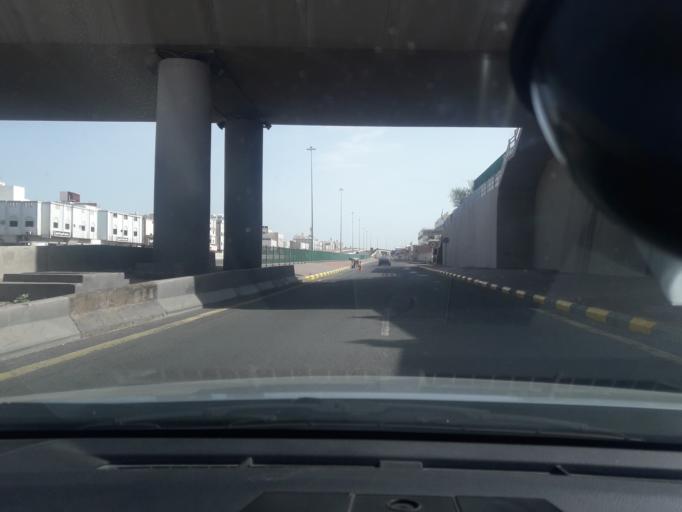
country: SA
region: Al Madinah al Munawwarah
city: Medina
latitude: 24.4484
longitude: 39.6593
